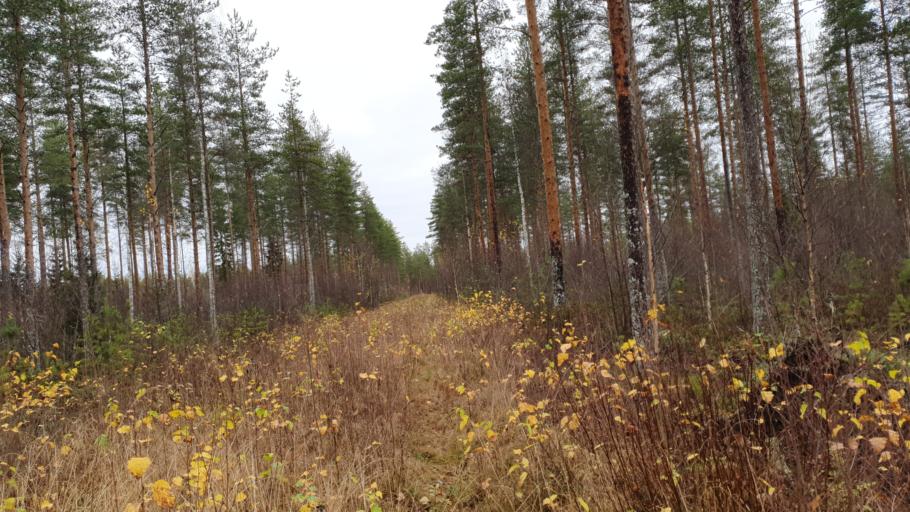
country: FI
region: Kainuu
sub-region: Kehys-Kainuu
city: Kuhmo
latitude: 64.1413
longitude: 29.4183
